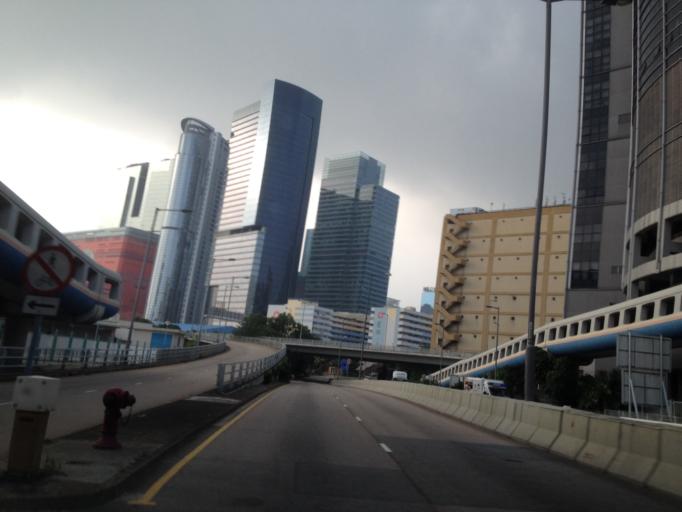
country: HK
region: Kowloon City
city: Kowloon
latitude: 22.3174
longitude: 114.2135
